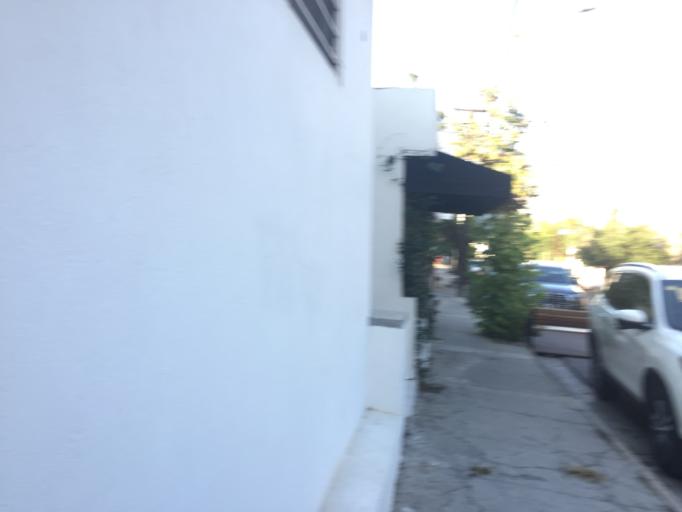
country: MX
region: Nuevo Leon
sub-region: San Pedro Garza Garcia
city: San Pedro Garza Garcia
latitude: 25.6613
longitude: -100.4020
